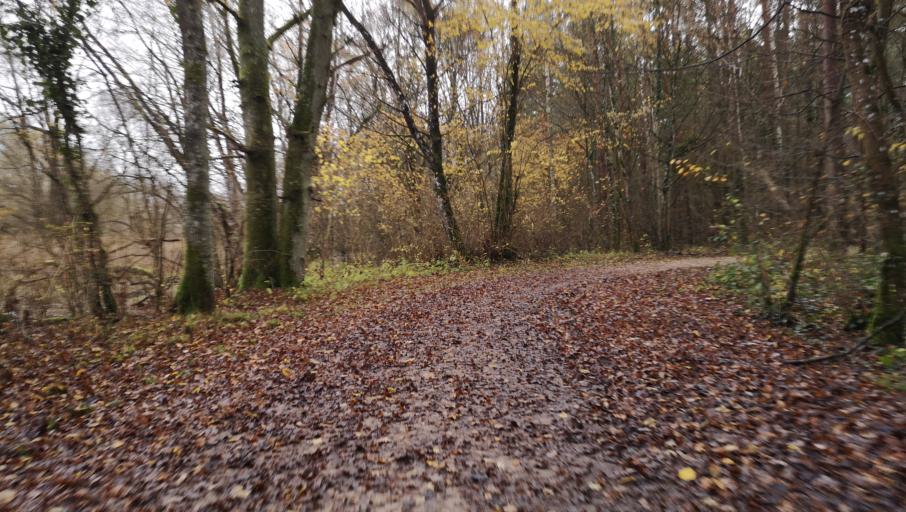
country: FR
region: Centre
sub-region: Departement du Loiret
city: Boigny-sur-Bionne
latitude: 47.9421
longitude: 1.9969
